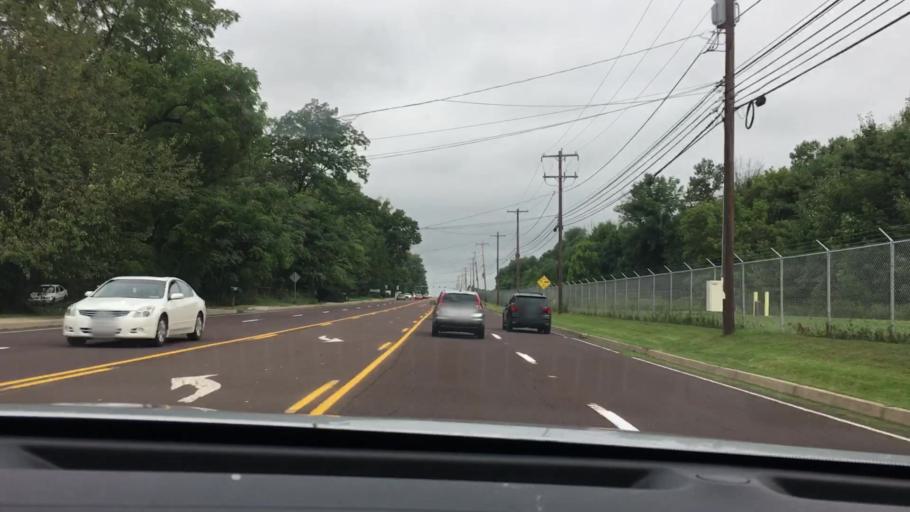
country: US
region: Pennsylvania
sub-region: Montgomery County
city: Horsham
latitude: 40.1897
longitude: -75.1482
